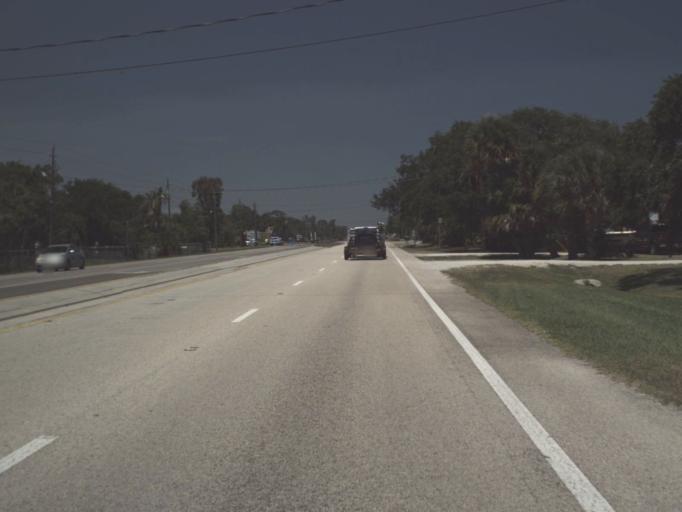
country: US
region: Florida
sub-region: Brevard County
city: Grant-Valkaria
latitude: 27.9323
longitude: -80.5278
